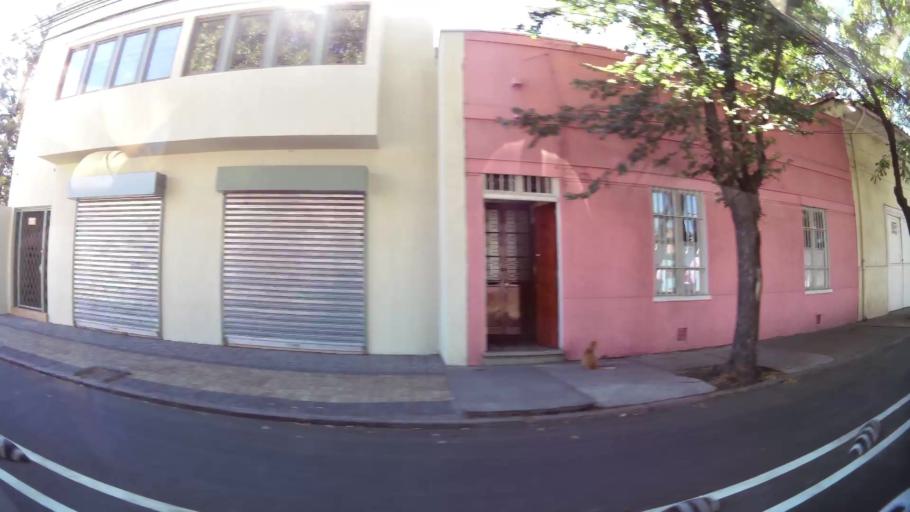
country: CL
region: O'Higgins
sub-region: Provincia de Cachapoal
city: Rancagua
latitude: -34.1724
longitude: -70.7383
